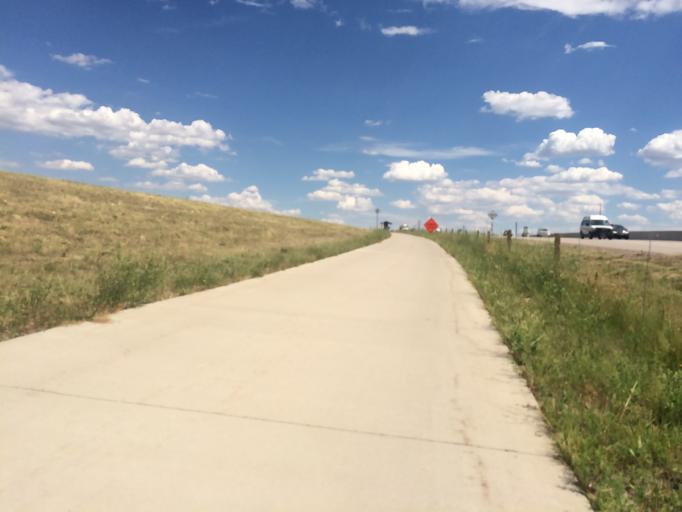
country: US
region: Colorado
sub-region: Boulder County
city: Superior
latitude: 39.9681
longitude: -105.1911
